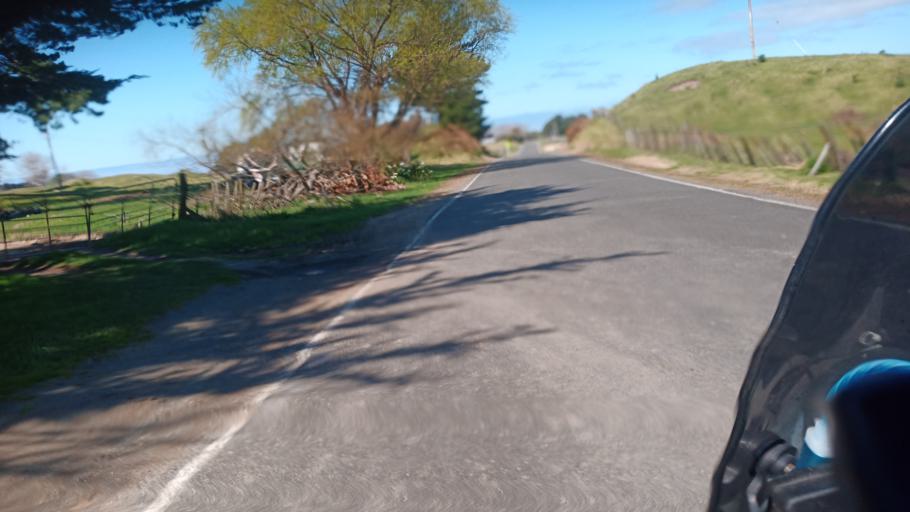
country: NZ
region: Gisborne
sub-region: Gisborne District
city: Gisborne
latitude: -39.0495
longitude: 177.8705
